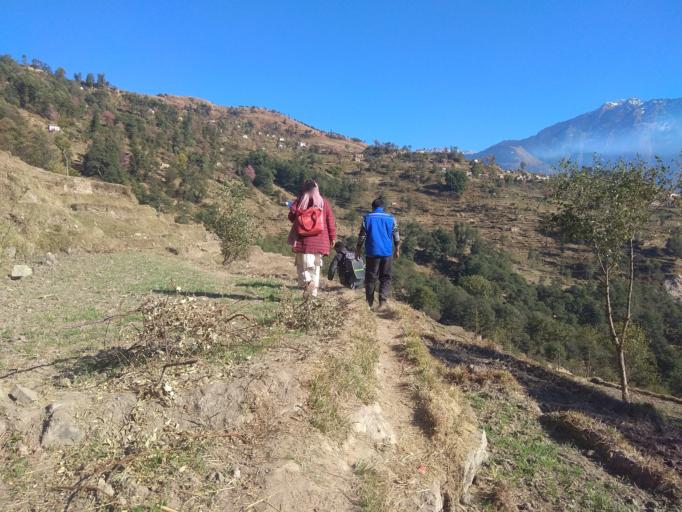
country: NP
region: Far Western
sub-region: Seti Zone
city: Achham
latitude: 29.2562
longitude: 81.6381
